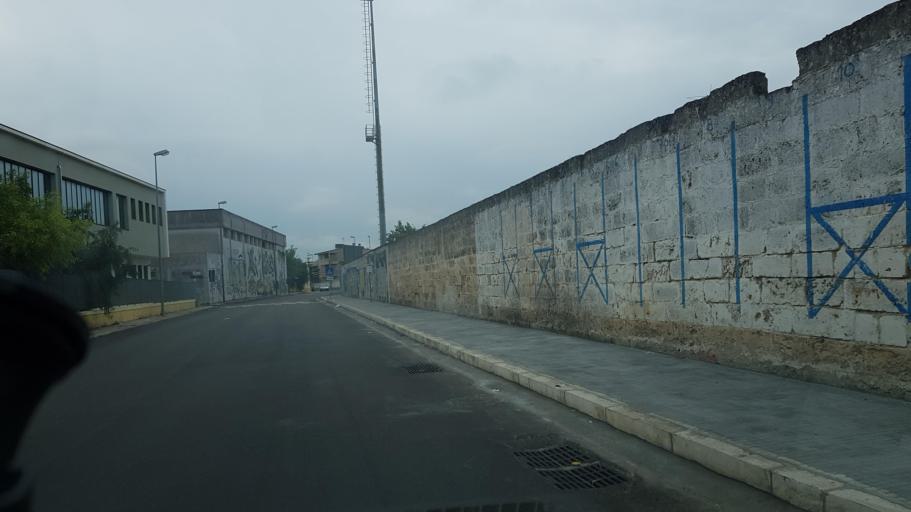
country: IT
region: Apulia
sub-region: Provincia di Brindisi
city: Cellino San Marco
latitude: 40.4737
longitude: 17.9601
